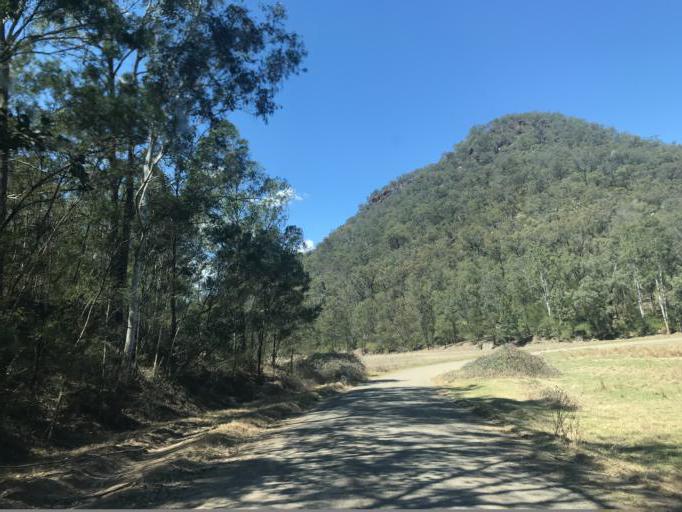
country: AU
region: New South Wales
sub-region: Hornsby Shire
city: Glenorie
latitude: -33.2119
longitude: 150.9791
